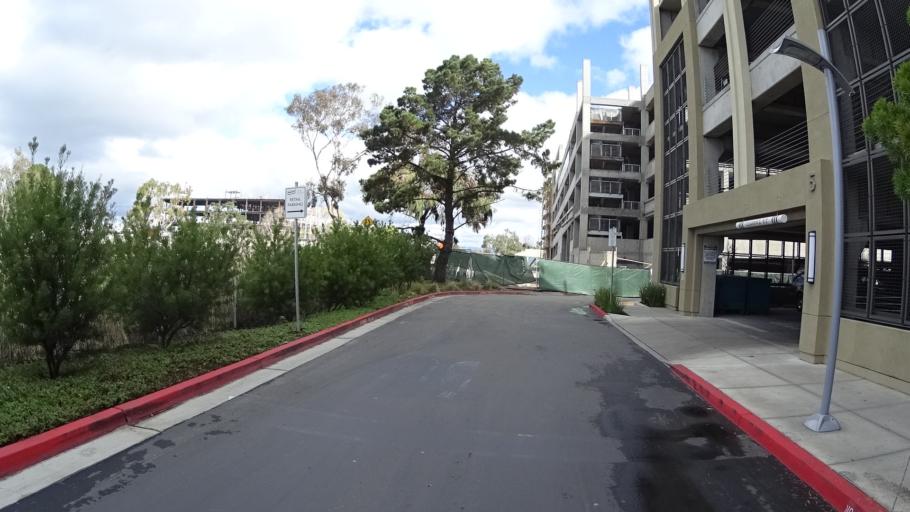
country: US
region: California
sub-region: San Mateo County
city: Foster City
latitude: 37.5656
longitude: -122.2707
